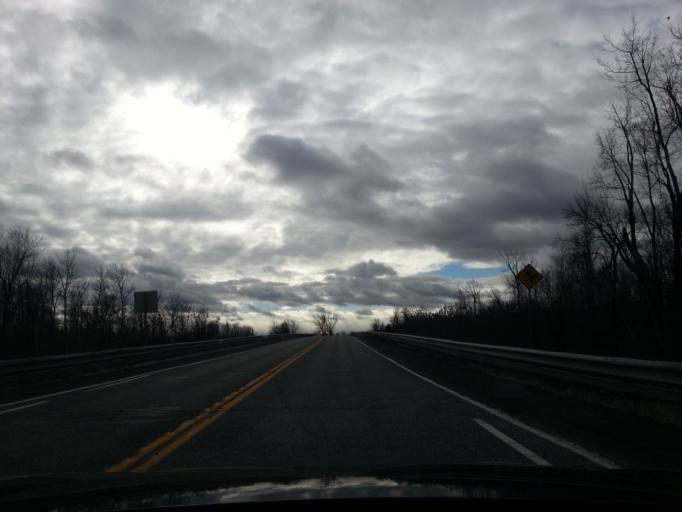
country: CA
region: Ontario
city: Bells Corners
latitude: 45.1964
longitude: -75.7232
